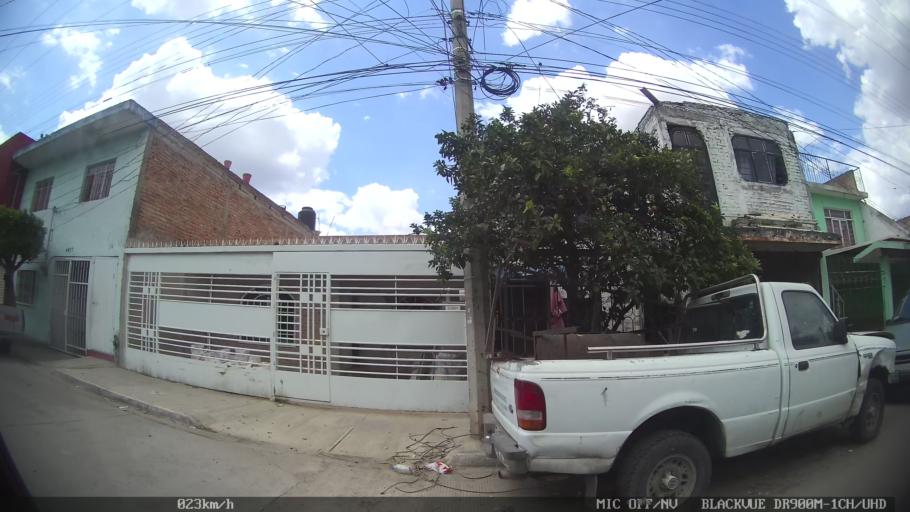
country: MX
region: Jalisco
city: Tlaquepaque
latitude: 20.6522
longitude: -103.2734
